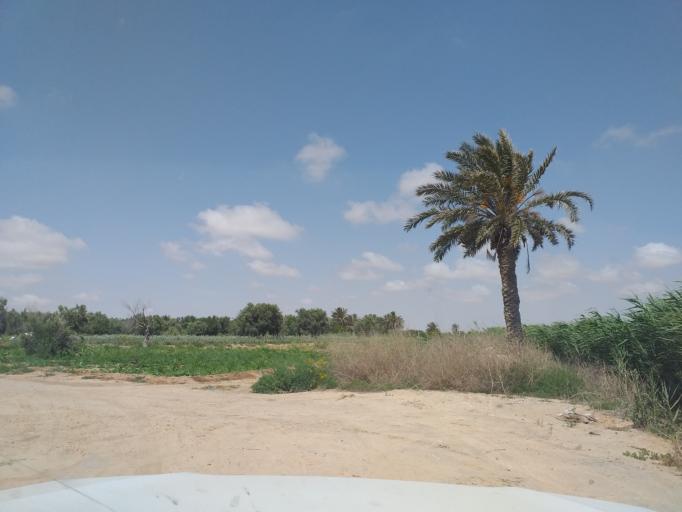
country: TN
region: Qabis
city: Gabes
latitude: 33.9505
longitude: 10.0545
